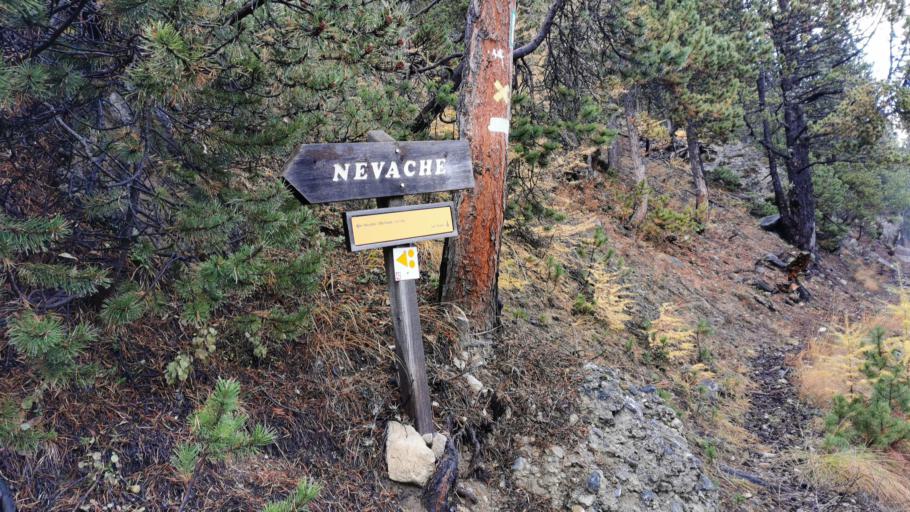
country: IT
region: Piedmont
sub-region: Provincia di Torino
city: Bardonecchia
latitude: 45.0307
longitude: 6.6292
